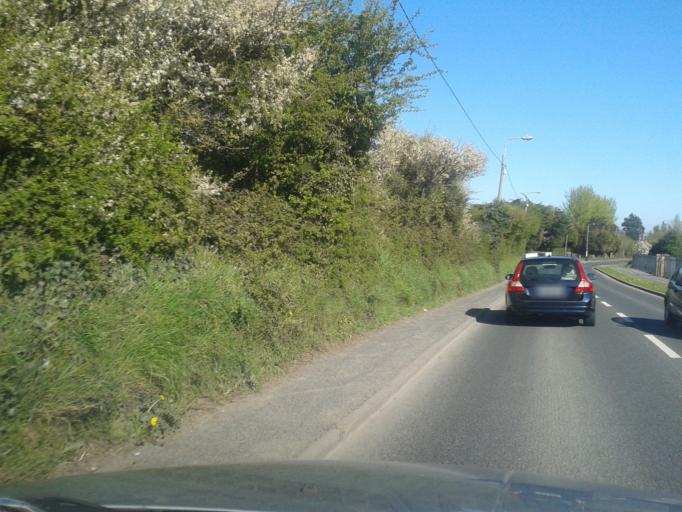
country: IE
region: Leinster
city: Kinsealy-Drinan
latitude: 53.4526
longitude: -6.1953
